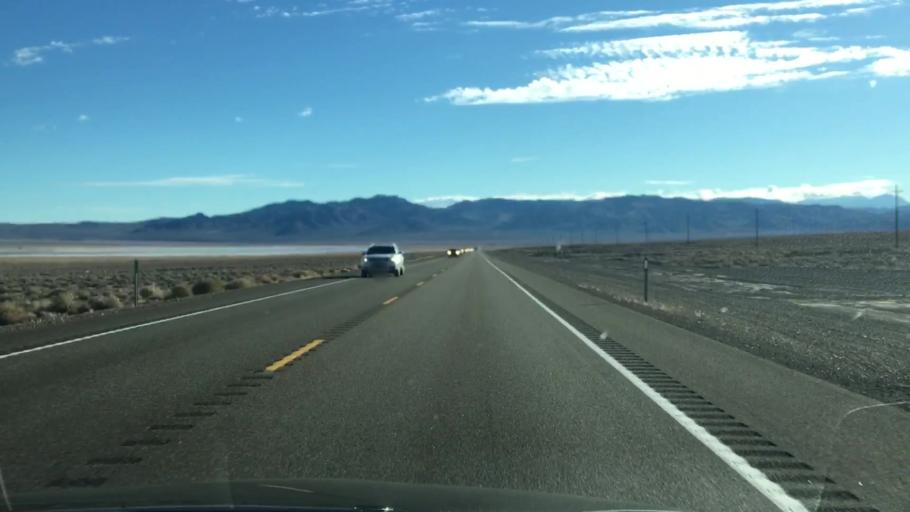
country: US
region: Nevada
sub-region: Mineral County
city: Hawthorne
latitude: 38.3211
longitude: -118.1028
